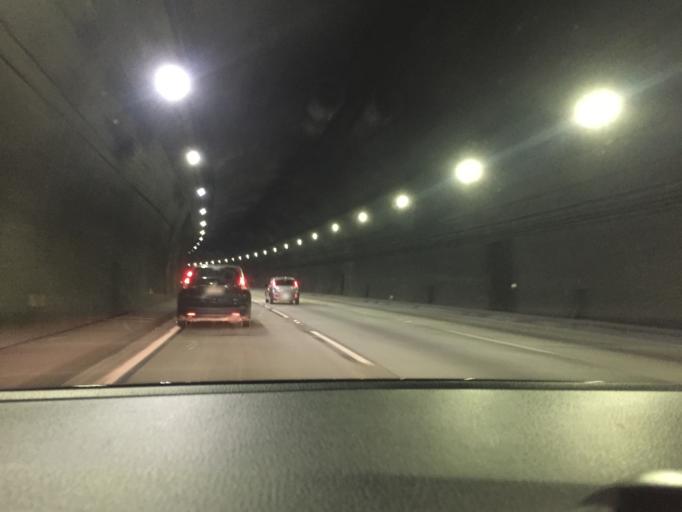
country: BR
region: Sao Paulo
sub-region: Cubatao
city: Cubatao
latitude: -23.8892
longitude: -46.5027
